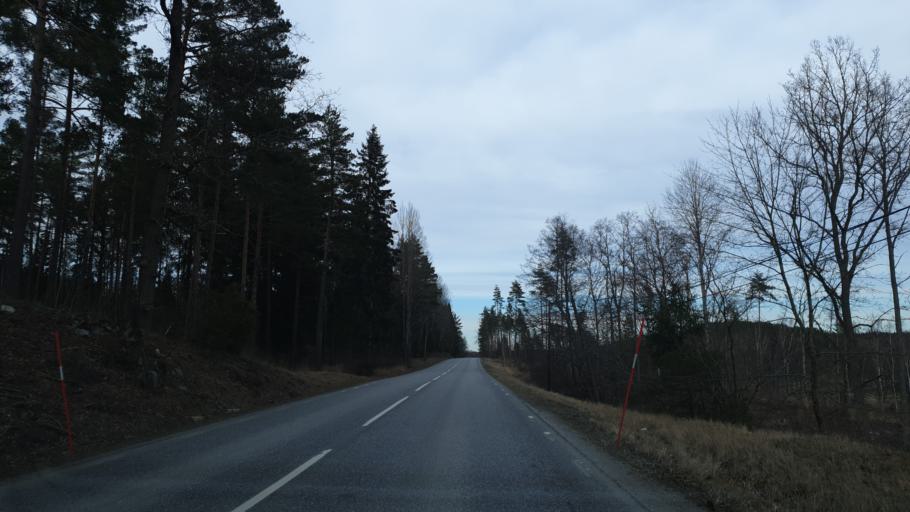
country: SE
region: Stockholm
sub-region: Osterakers Kommun
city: Akersberga
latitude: 59.5902
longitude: 18.2991
